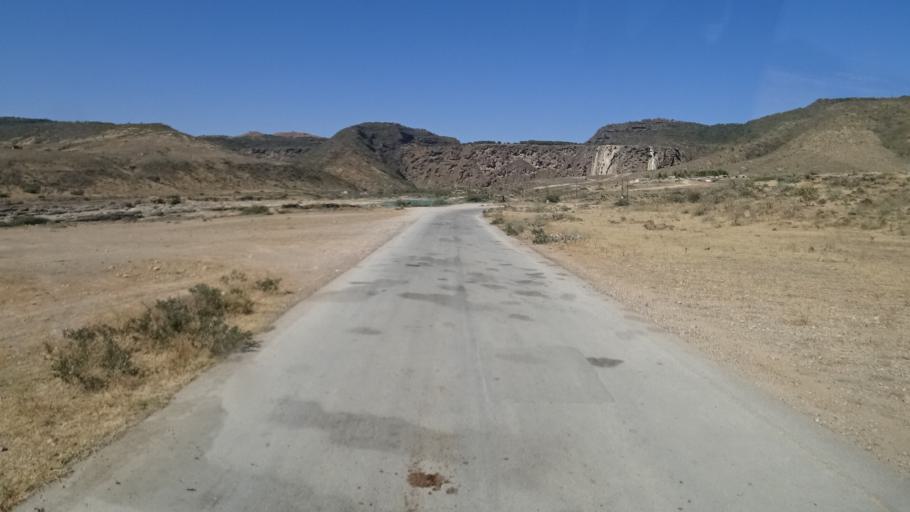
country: OM
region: Zufar
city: Salalah
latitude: 17.0657
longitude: 54.4310
